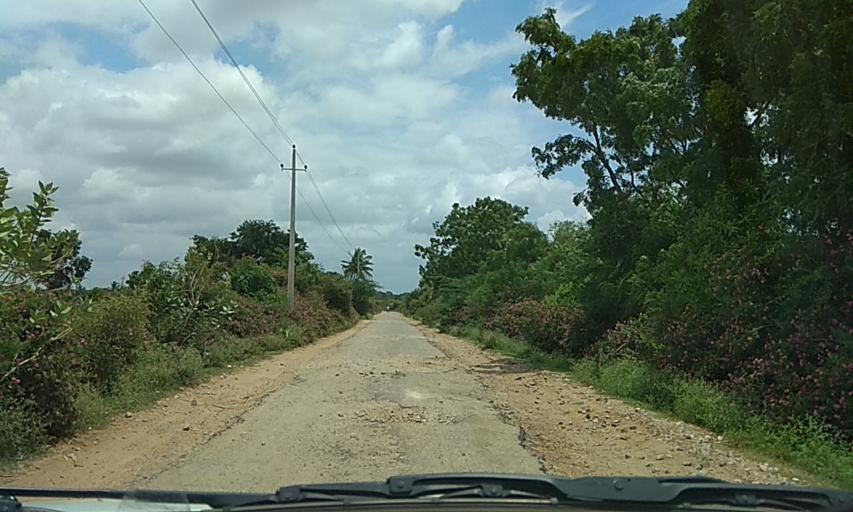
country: IN
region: Karnataka
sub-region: Chamrajnagar
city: Gundlupet
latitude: 11.8857
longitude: 76.6857
